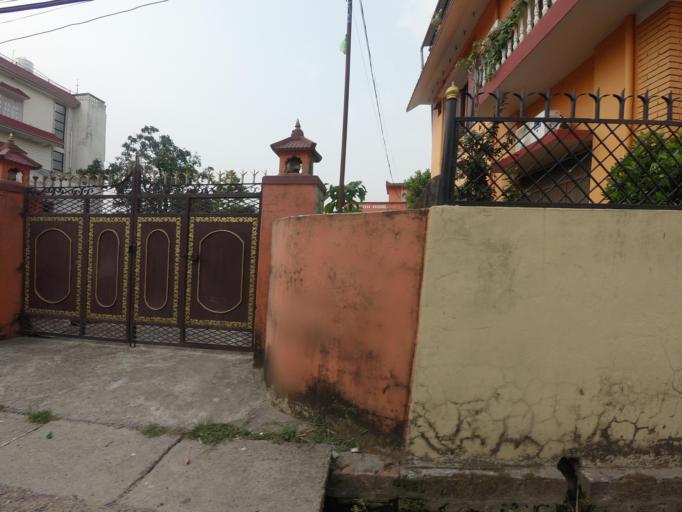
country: NP
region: Western Region
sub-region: Lumbini Zone
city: Bhairahawa
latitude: 27.4974
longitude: 83.4486
